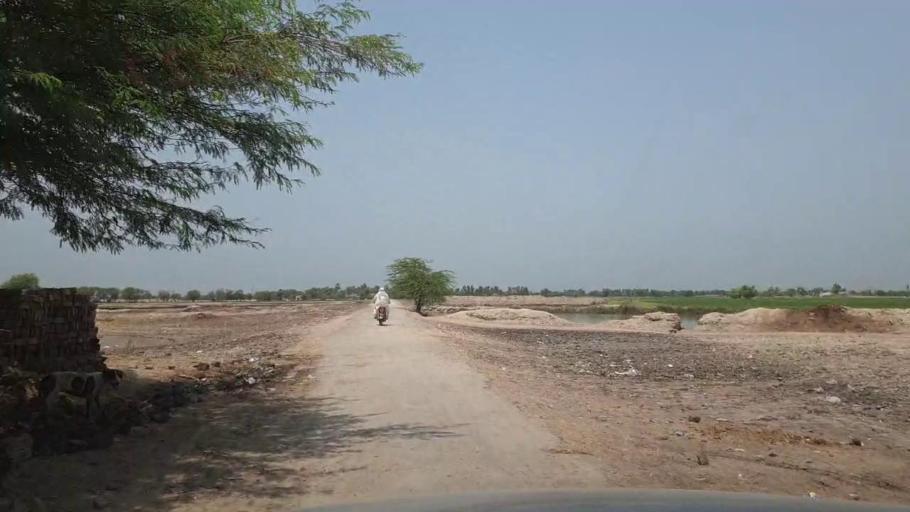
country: PK
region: Sindh
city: Garhi Yasin
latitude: 27.8651
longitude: 68.4578
